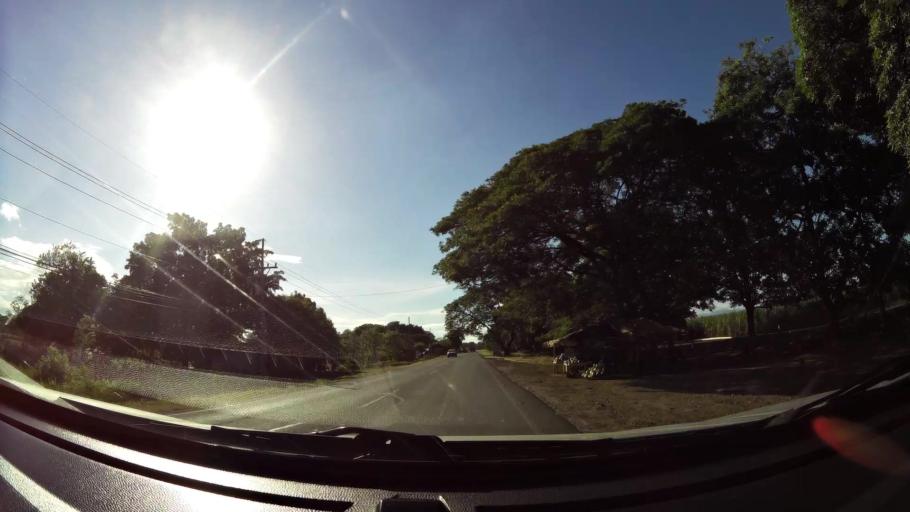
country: CR
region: Guanacaste
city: Belen
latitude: 10.4821
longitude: -85.5660
